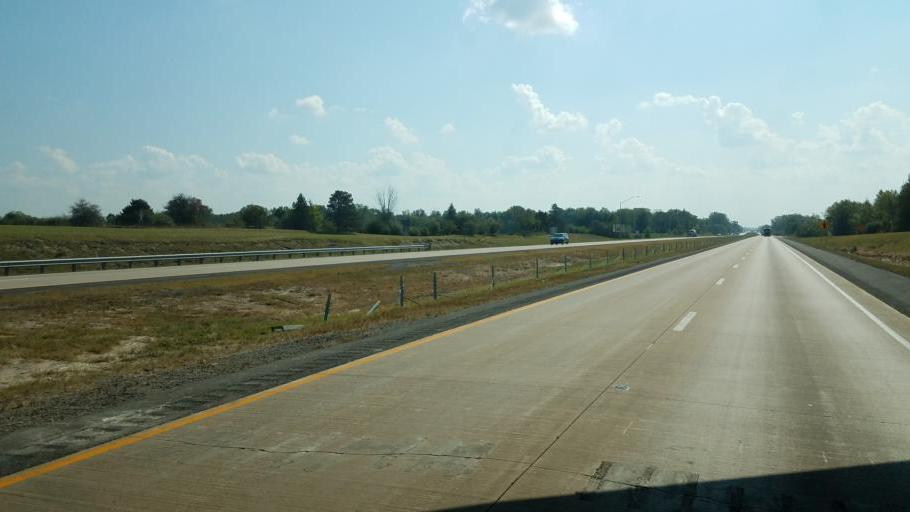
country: US
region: Indiana
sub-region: DeKalb County
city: Auburn
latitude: 41.3272
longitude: -85.0880
